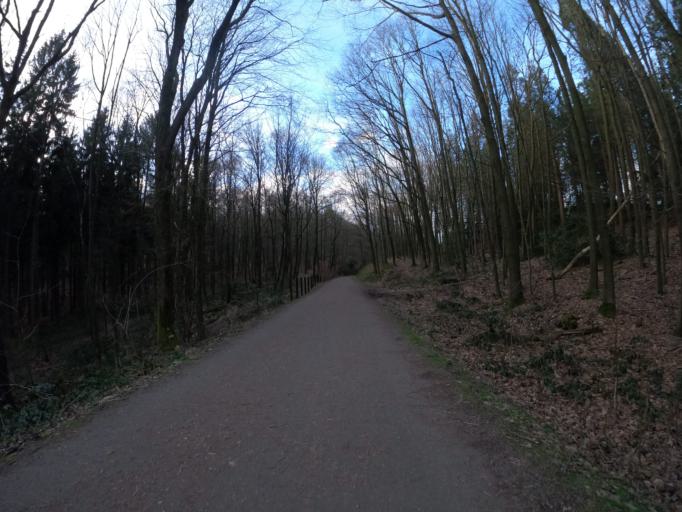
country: DE
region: North Rhine-Westphalia
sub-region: Regierungsbezirk Dusseldorf
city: Wuppertal
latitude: 51.2286
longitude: 7.1236
